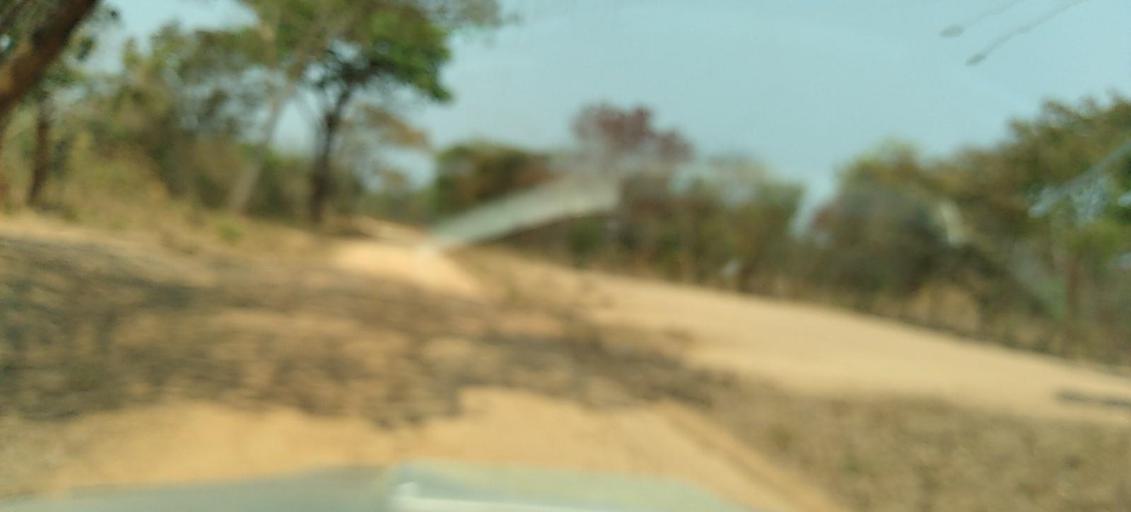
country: ZM
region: North-Western
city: Kasempa
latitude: -13.6667
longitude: 26.2868
